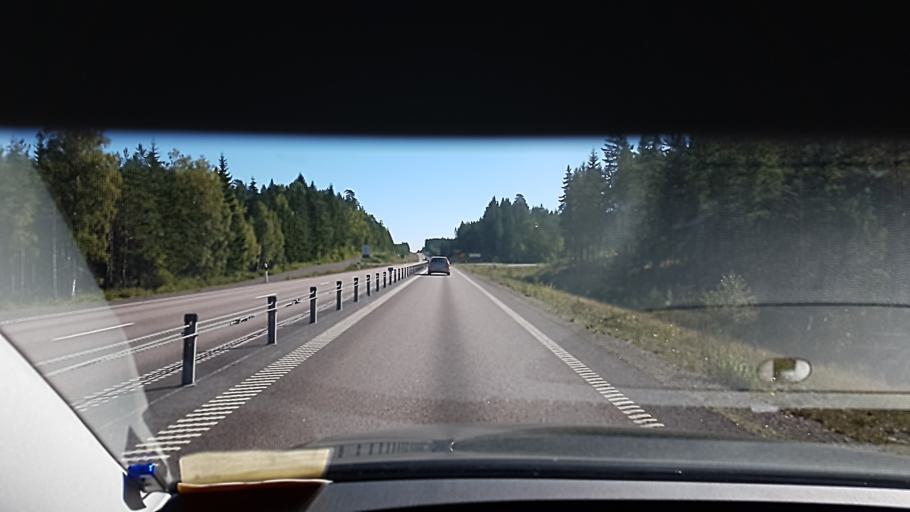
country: SE
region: Kalmar
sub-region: Emmaboda Kommun
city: Emmaboda
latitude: 56.7230
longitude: 15.5968
